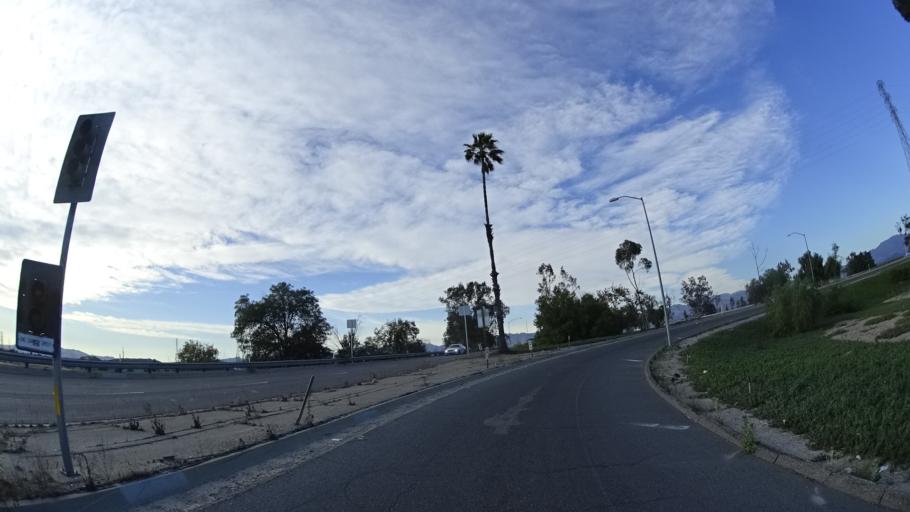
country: US
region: California
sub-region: Los Angeles County
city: Van Nuys
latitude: 34.2225
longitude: -118.4120
